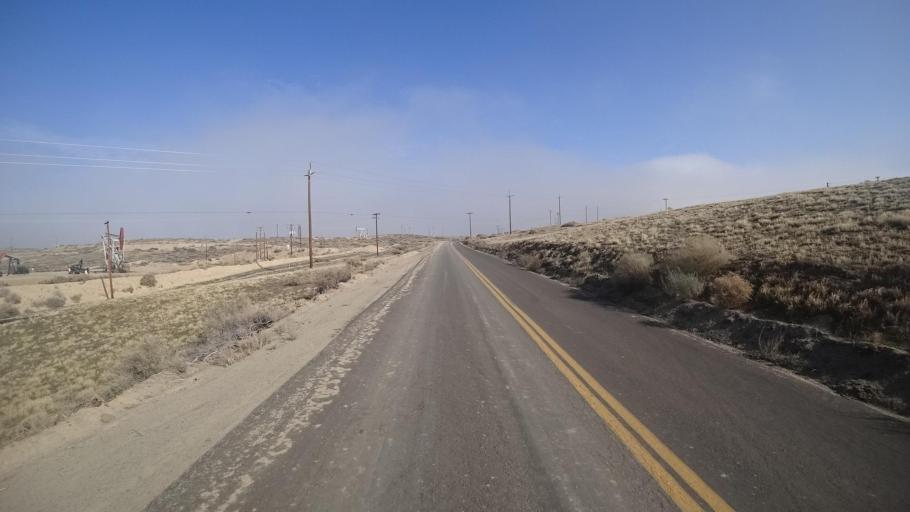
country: US
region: California
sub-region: Kern County
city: Ford City
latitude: 35.1644
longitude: -119.4155
